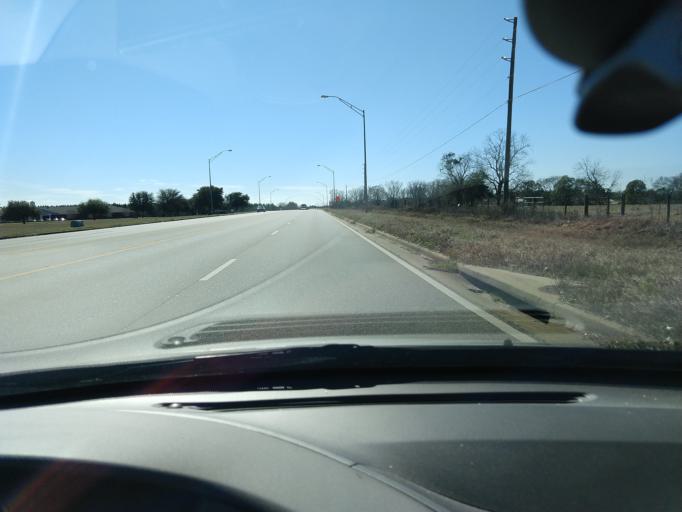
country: US
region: Alabama
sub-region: Covington County
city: Andalusia
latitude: 31.2871
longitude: -86.5041
